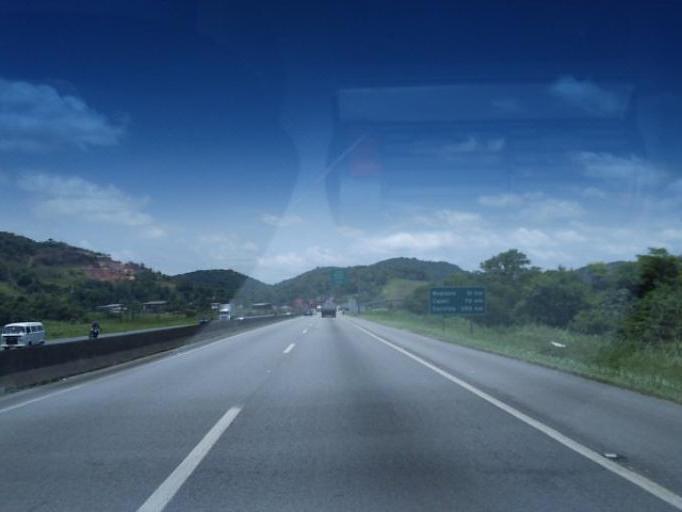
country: BR
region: Sao Paulo
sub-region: Juquia
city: Juquia
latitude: -24.3453
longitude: -47.6487
